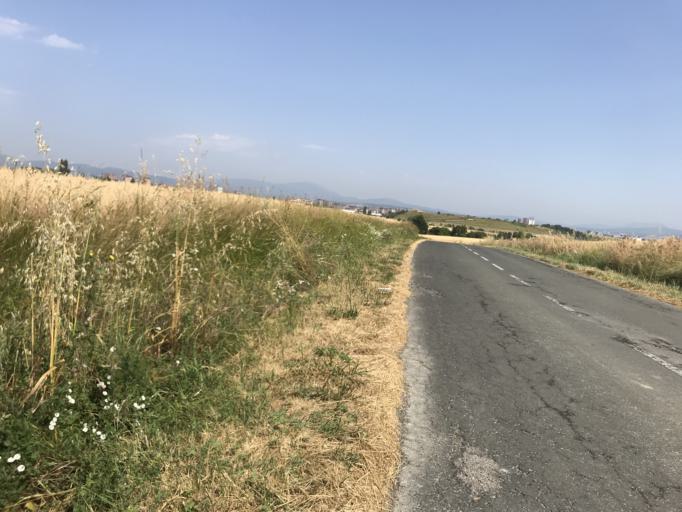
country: ES
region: Basque Country
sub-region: Provincia de Alava
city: Gasteiz / Vitoria
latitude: 42.8216
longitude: -2.6476
